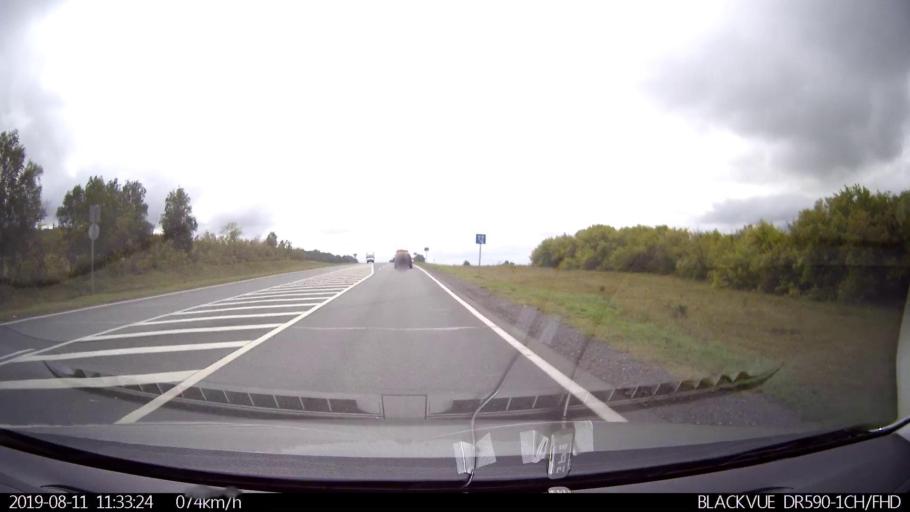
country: RU
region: Ulyanovsk
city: Krasnyy Gulyay
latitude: 54.0277
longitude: 48.2123
